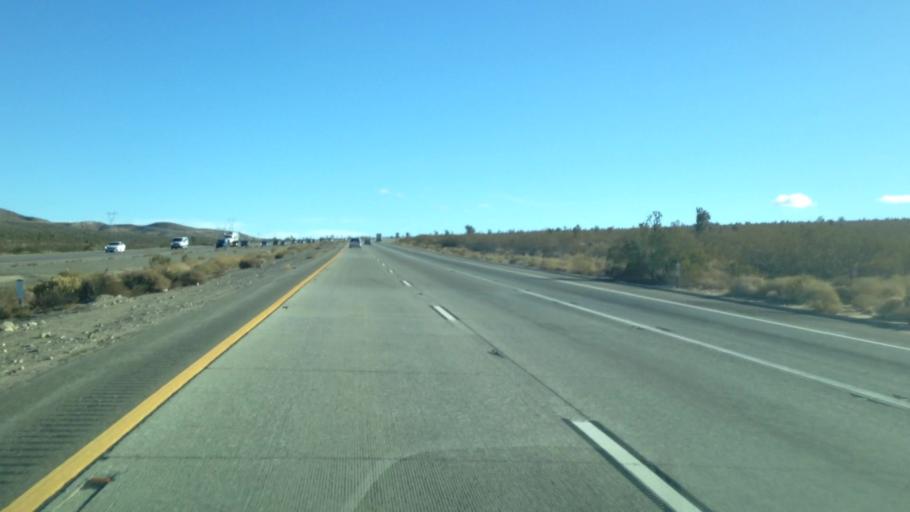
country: US
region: Nevada
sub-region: Clark County
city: Sandy Valley
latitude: 35.3918
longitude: -115.8346
